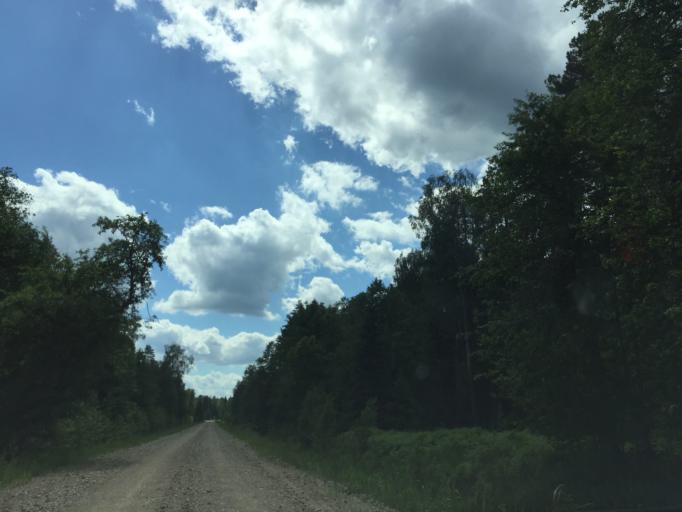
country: LV
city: Tireli
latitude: 56.8412
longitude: 23.6986
